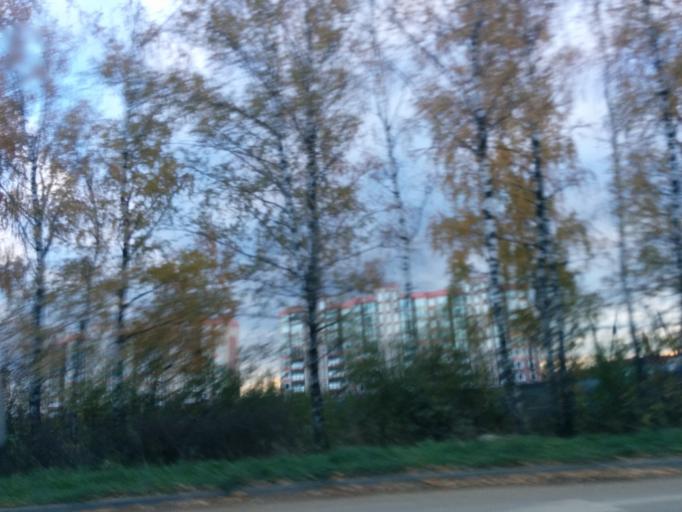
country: RU
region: Moscow
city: Zagor'ye
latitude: 55.5364
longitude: 37.6412
